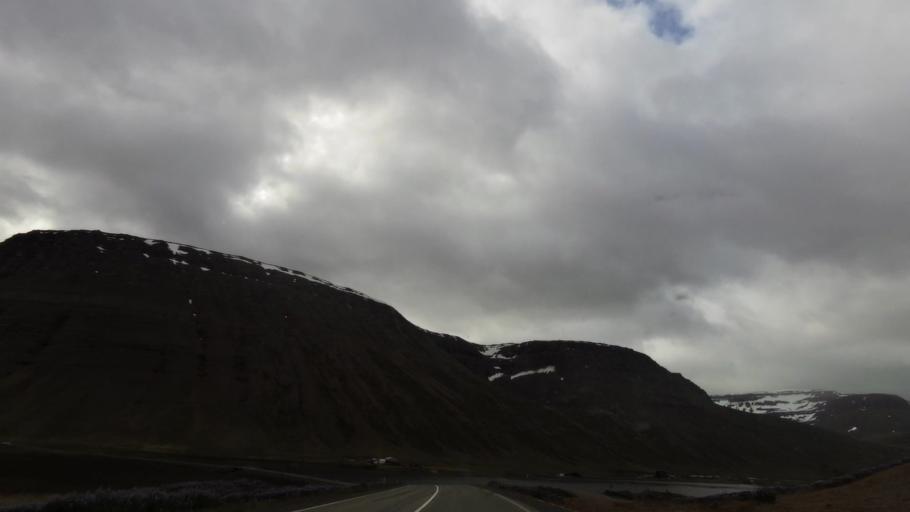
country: IS
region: Westfjords
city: Isafjoerdur
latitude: 66.0554
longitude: -23.1644
